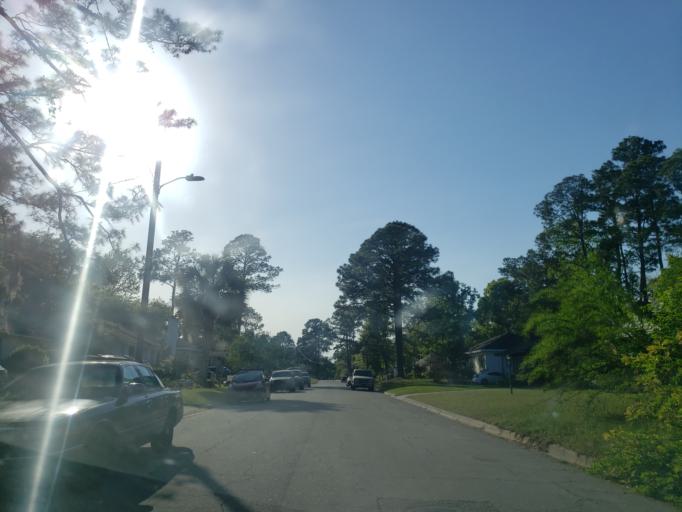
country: US
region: Georgia
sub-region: Chatham County
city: Thunderbolt
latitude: 32.0375
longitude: -81.0802
